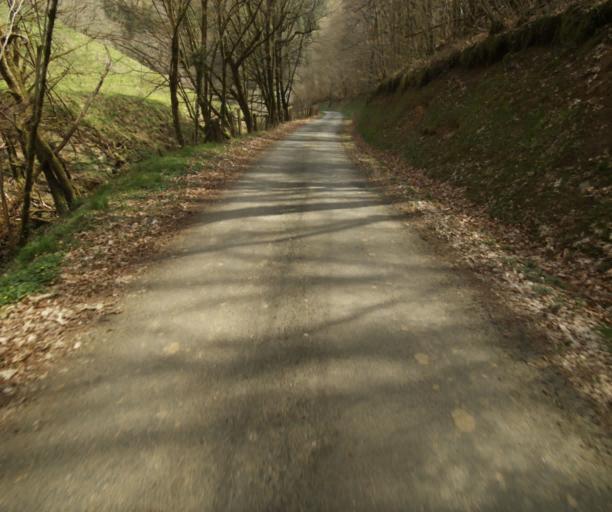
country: FR
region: Limousin
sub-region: Departement de la Correze
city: Naves
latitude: 45.3720
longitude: 1.7856
